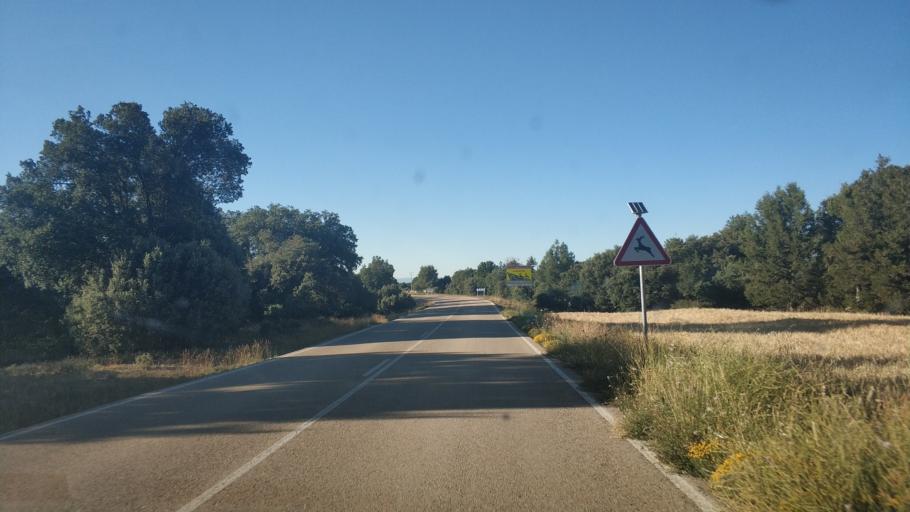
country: ES
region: Castille and Leon
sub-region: Provincia de Soria
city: Liceras
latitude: 41.4562
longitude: -3.2114
